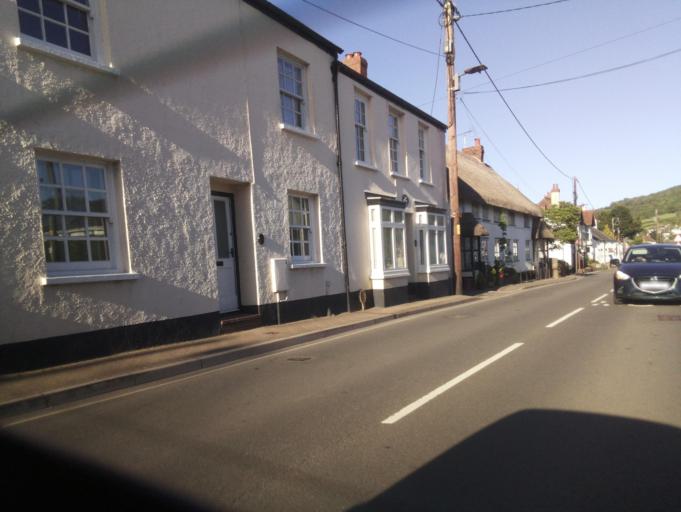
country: GB
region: England
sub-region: Devon
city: Sidmouth
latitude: 50.7033
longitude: -3.2260
